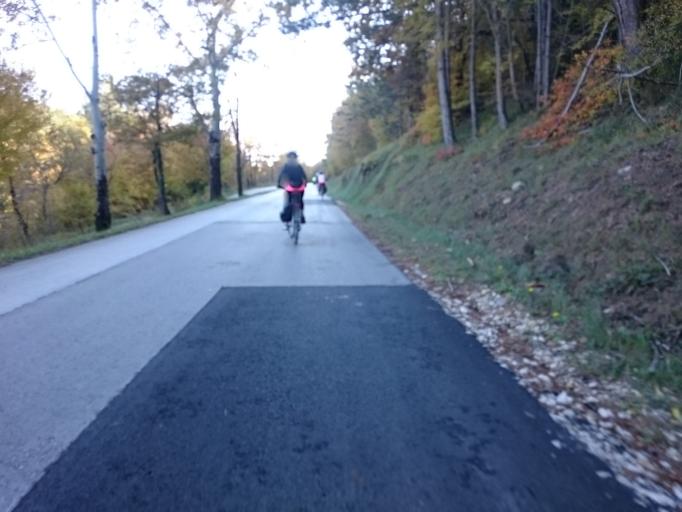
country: HR
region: Istarska
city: Buje
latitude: 45.3886
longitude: 13.7223
